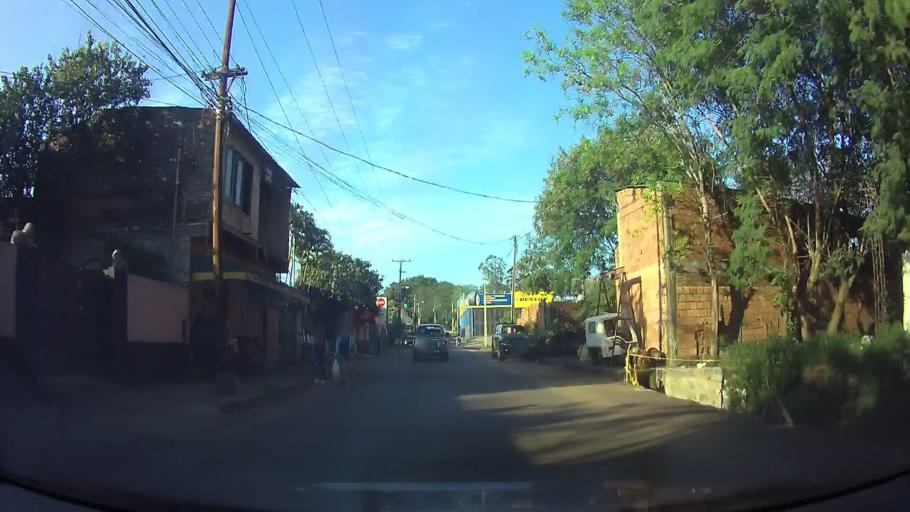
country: PY
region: Central
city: Fernando de la Mora
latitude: -25.3381
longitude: -57.5299
